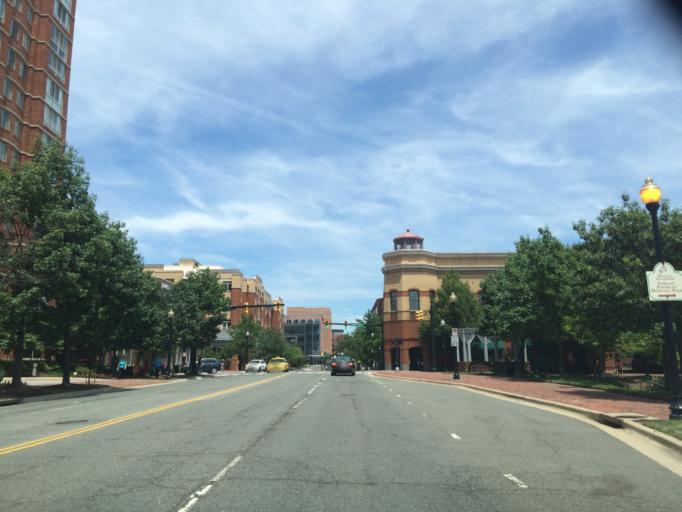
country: US
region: Virginia
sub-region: City of Alexandria
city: Alexandria
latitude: 38.8025
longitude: -77.0599
